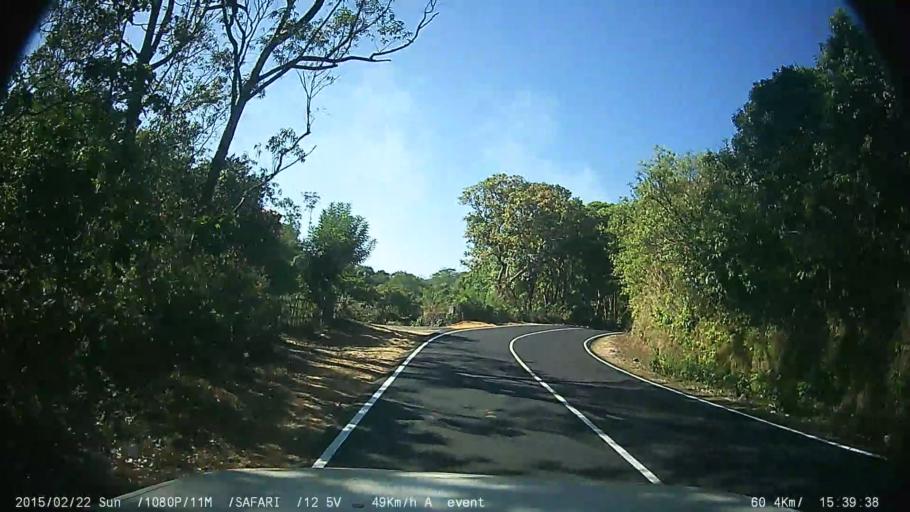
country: IN
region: Kerala
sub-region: Kottayam
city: Erattupetta
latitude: 9.5656
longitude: 76.9780
